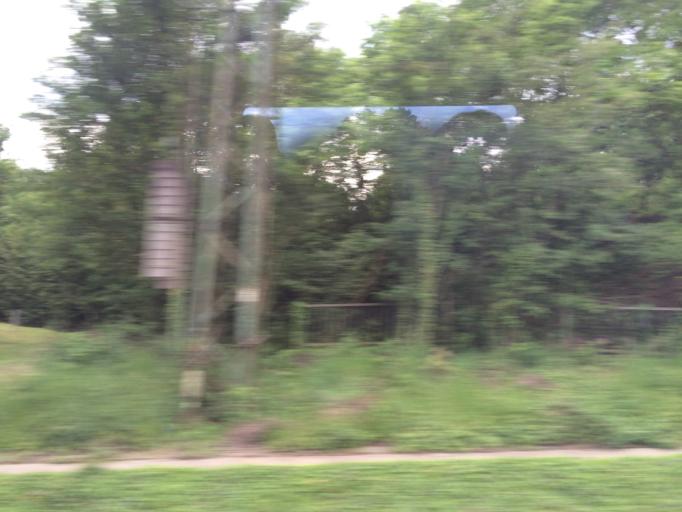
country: DE
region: Hesse
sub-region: Regierungsbezirk Darmstadt
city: Hanau am Main
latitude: 50.1264
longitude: 8.9173
